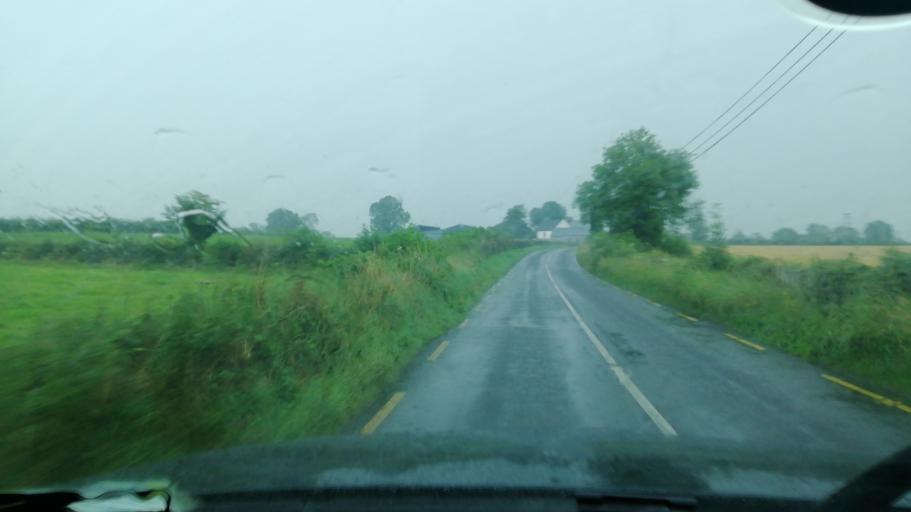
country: IE
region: Leinster
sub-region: Kilkenny
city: Kilkenny
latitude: 52.6095
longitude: -7.2663
